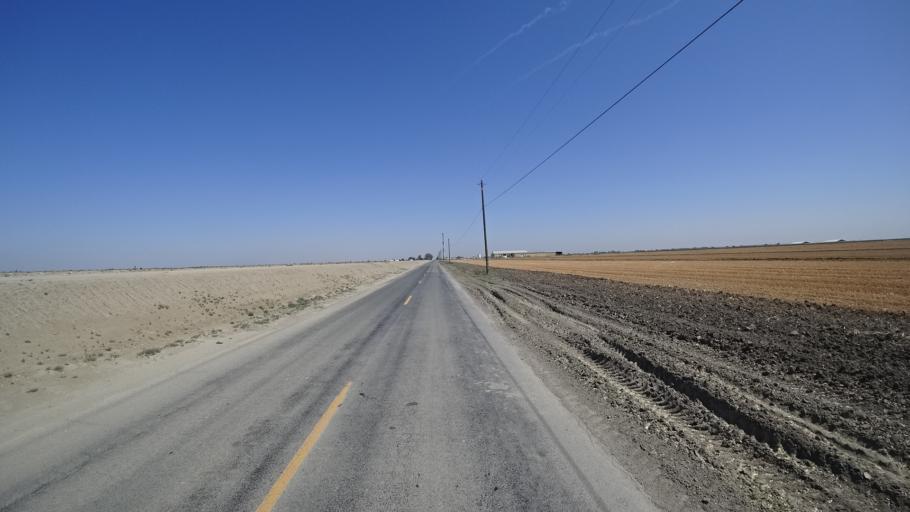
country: US
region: California
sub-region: Kings County
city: Corcoran
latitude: 36.0175
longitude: -119.5361
